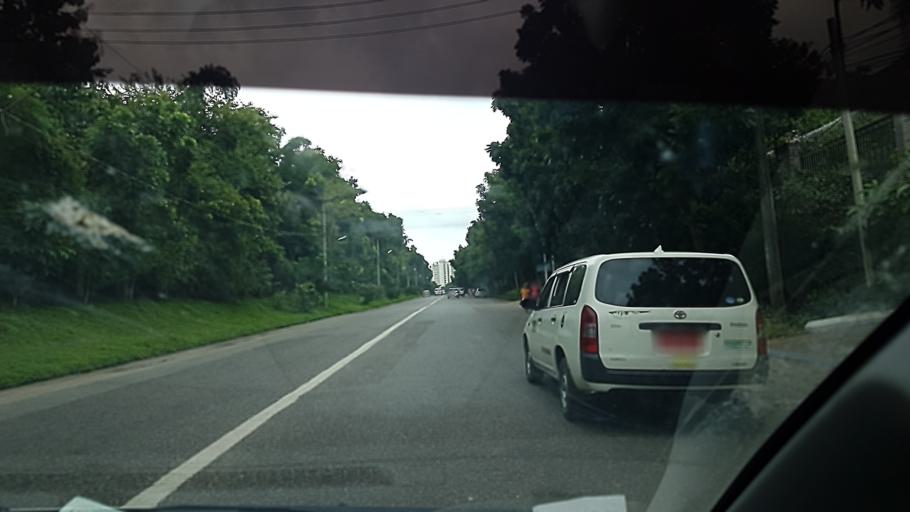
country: MM
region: Yangon
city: Yangon
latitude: 16.7944
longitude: 96.1320
